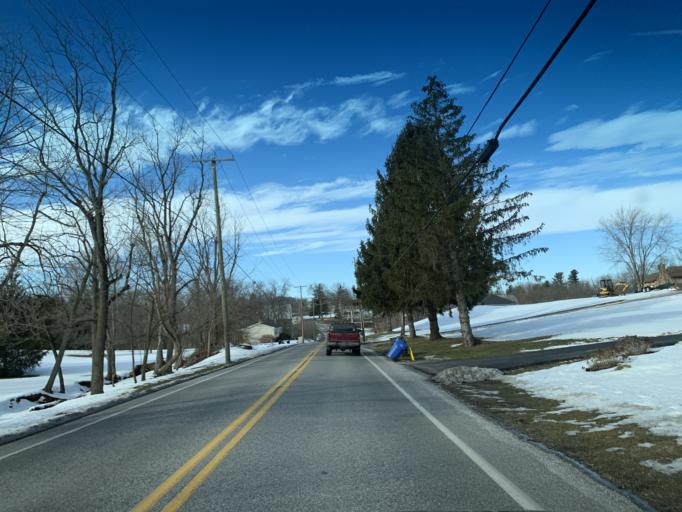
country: US
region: Pennsylvania
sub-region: York County
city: Weigelstown
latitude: 39.9569
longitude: -76.8347
